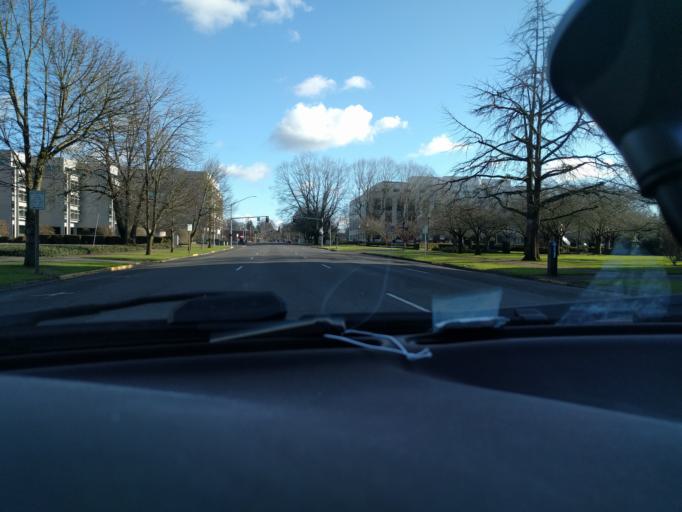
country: US
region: Oregon
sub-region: Marion County
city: Salem
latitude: 44.9416
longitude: -123.0302
